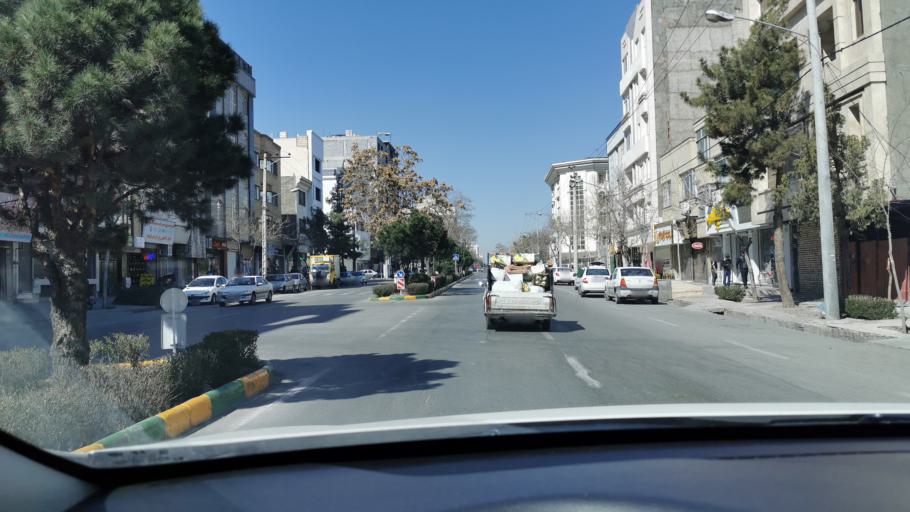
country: IR
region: Razavi Khorasan
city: Mashhad
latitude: 36.3277
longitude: 59.5160
